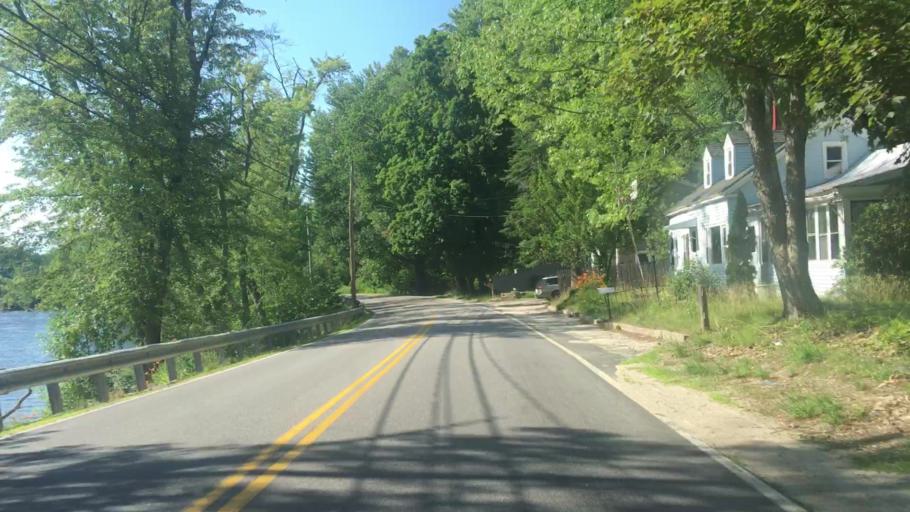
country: US
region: Maine
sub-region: York County
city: Hollis Center
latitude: 43.6633
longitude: -70.5986
